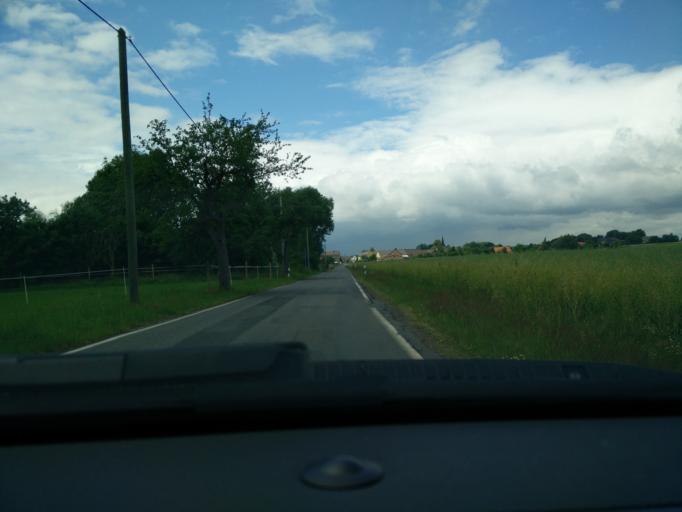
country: DE
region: Saxony
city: Grossbardau
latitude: 51.1796
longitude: 12.7002
